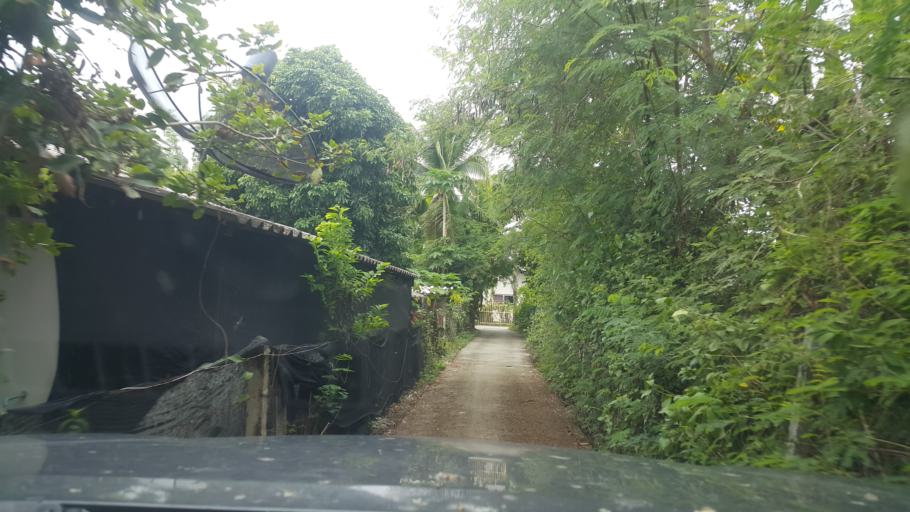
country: TH
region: Chiang Mai
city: Hang Dong
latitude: 18.6907
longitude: 98.8926
